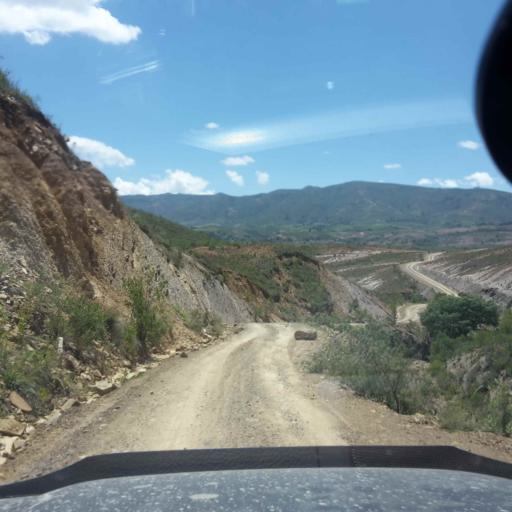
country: BO
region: Cochabamba
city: Totora
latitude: -17.7748
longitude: -65.2698
